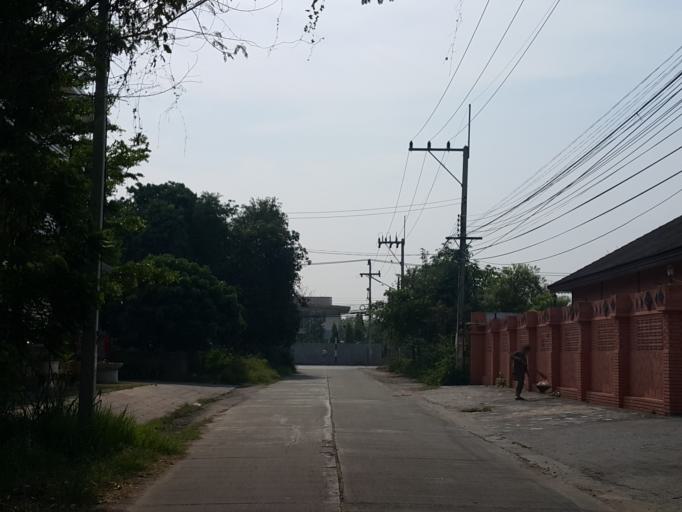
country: TH
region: Chiang Mai
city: Chiang Mai
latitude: 18.7602
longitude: 98.9876
